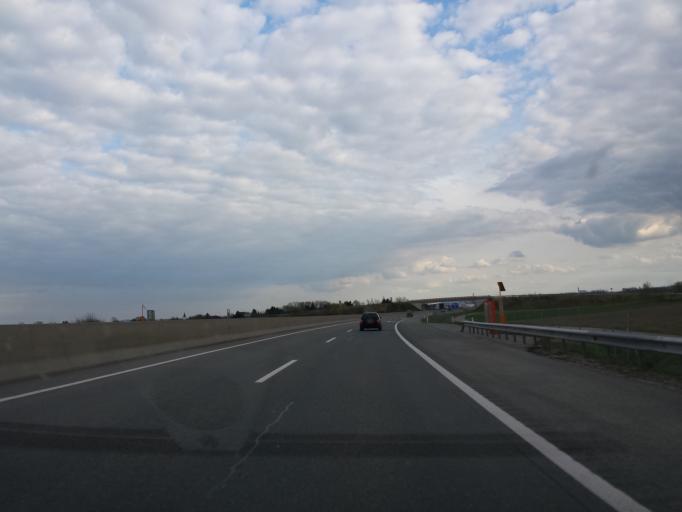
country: AT
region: Lower Austria
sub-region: Politischer Bezirk Tulln
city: Kirchberg am Wagram
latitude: 48.3960
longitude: 15.9149
